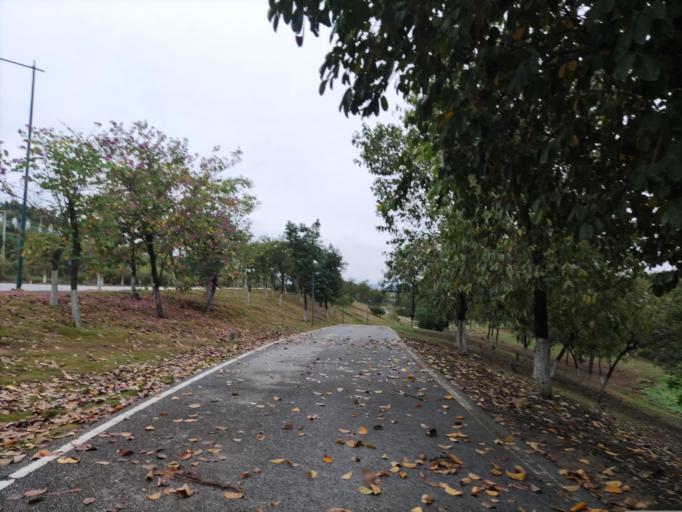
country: CN
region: Guangxi Zhuangzu Zizhiqu
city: Tianzhou
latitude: 23.7804
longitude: 106.7317
